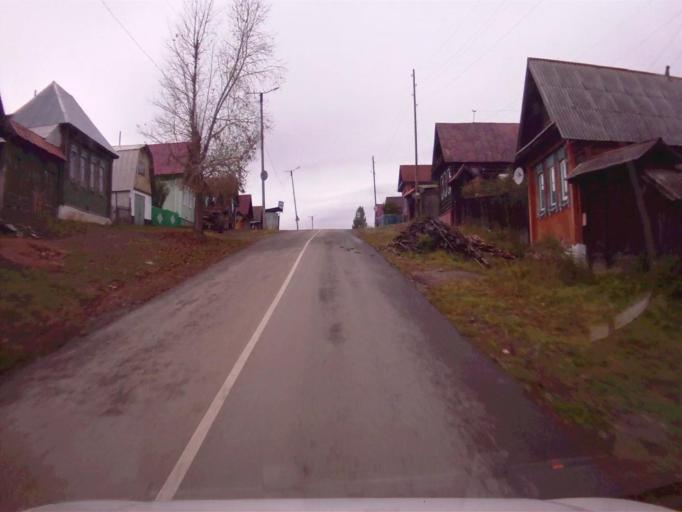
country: RU
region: Chelyabinsk
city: Nyazepetrovsk
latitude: 56.0619
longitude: 59.5759
